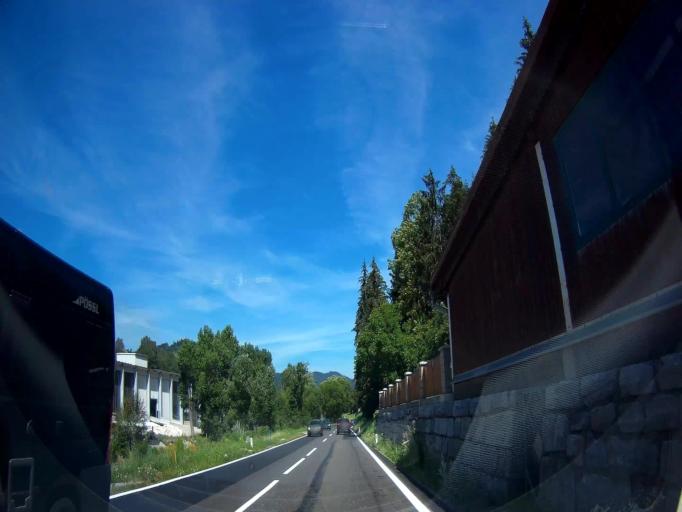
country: AT
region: Carinthia
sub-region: Politischer Bezirk Sankt Veit an der Glan
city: Micheldorf
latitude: 46.8968
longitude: 14.4439
